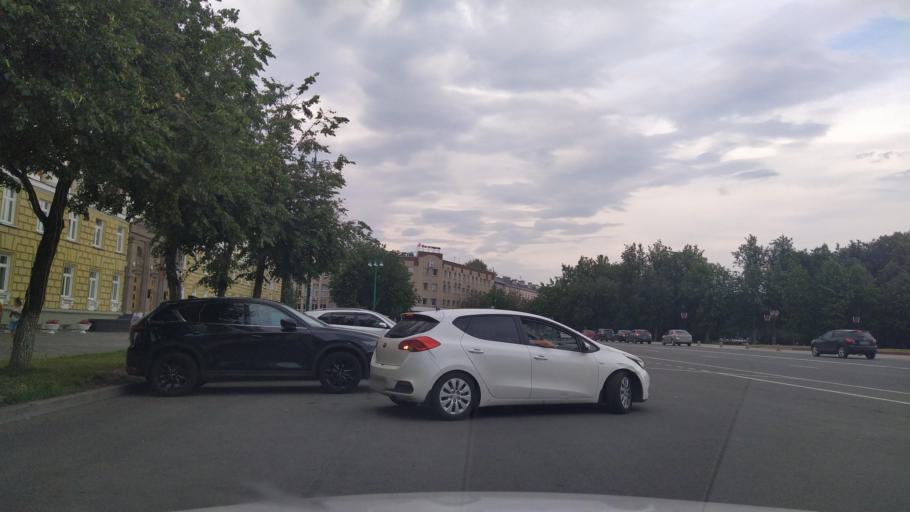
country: RU
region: Novgorod
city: Velikiy Novgorod
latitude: 58.5224
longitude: 31.2690
